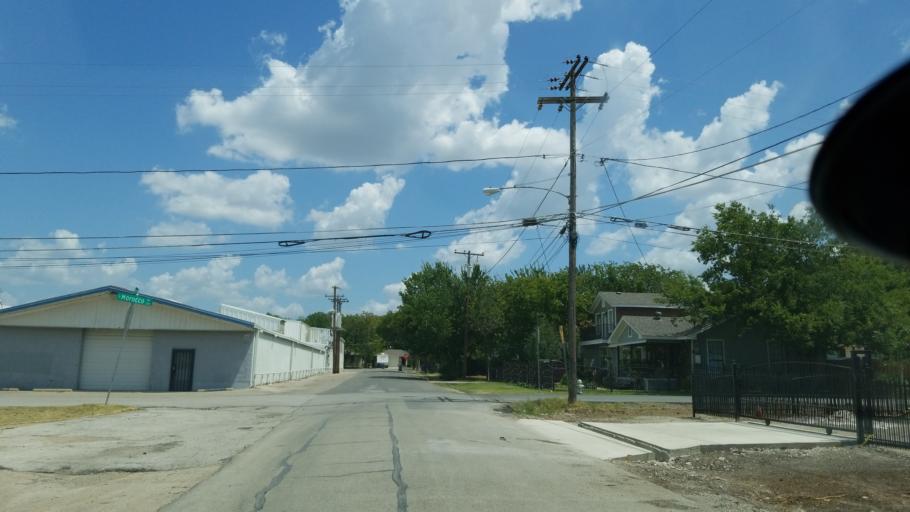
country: US
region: Texas
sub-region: Dallas County
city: Cockrell Hill
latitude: 32.7440
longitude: -96.9105
